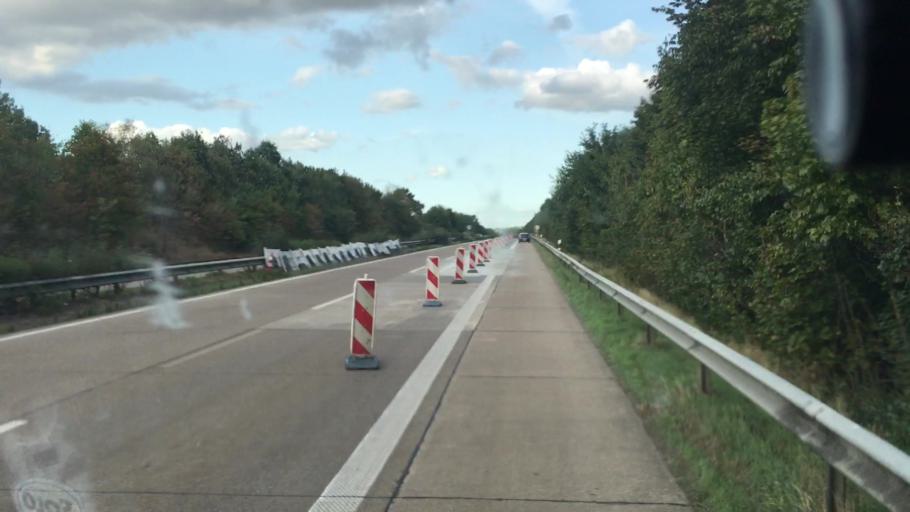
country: DE
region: Lower Saxony
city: Wardenburg
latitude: 53.0730
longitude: 8.2446
